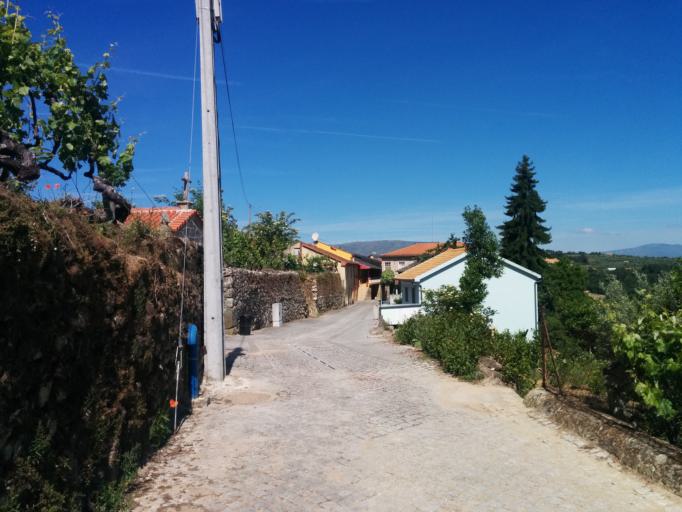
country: PT
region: Viseu
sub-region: Tarouca
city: Tarouca
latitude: 41.0444
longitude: -7.7426
